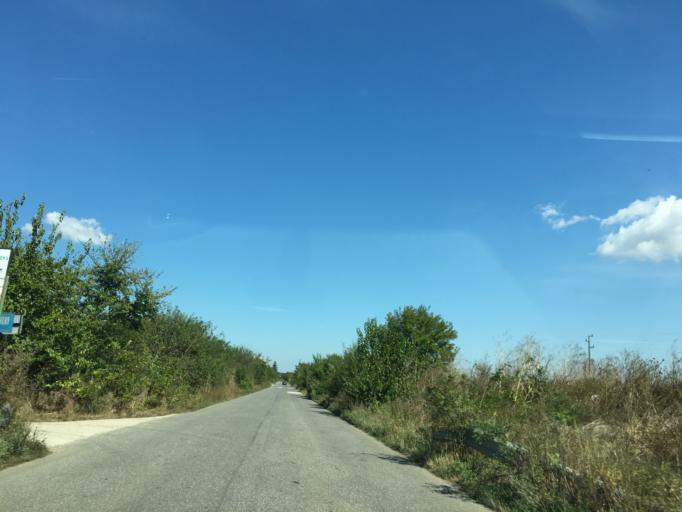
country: RO
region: Olt
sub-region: Comuna Orlea
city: Orlea
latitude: 43.6285
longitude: 24.3867
